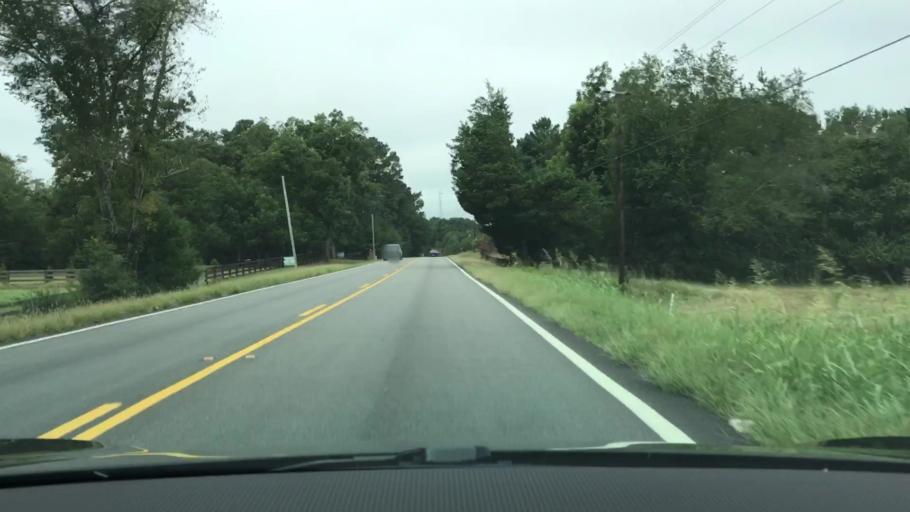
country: US
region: Georgia
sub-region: Greene County
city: Greensboro
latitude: 33.5674
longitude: -83.1592
